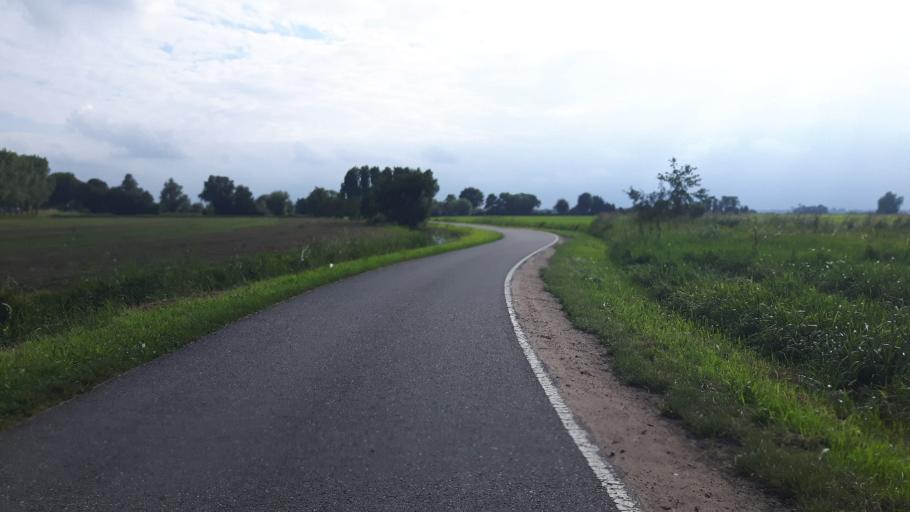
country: NL
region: Utrecht
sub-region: Gemeente De Ronde Venen
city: Mijdrecht
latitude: 52.1756
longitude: 4.9044
